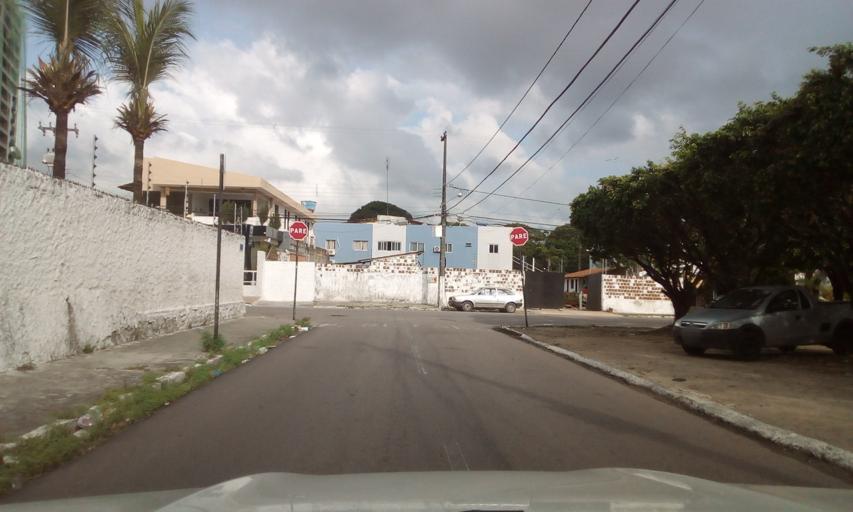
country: BR
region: Paraiba
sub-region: Joao Pessoa
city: Joao Pessoa
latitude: -7.1459
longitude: -34.8477
